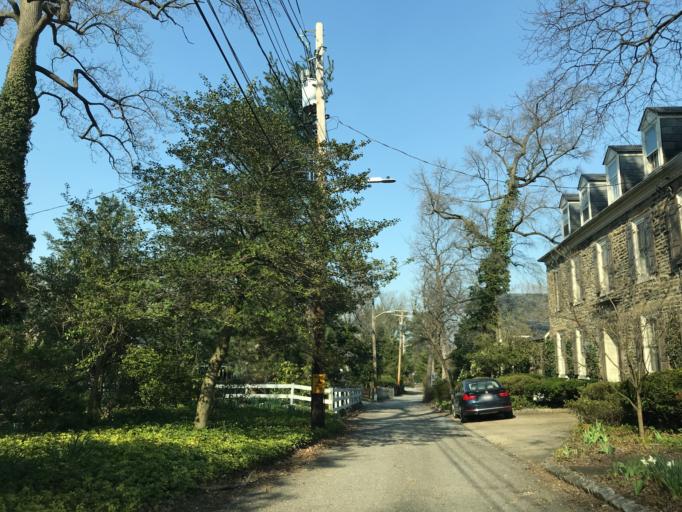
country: US
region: Maryland
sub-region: Baltimore County
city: Towson
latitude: 39.3638
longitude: -76.6200
